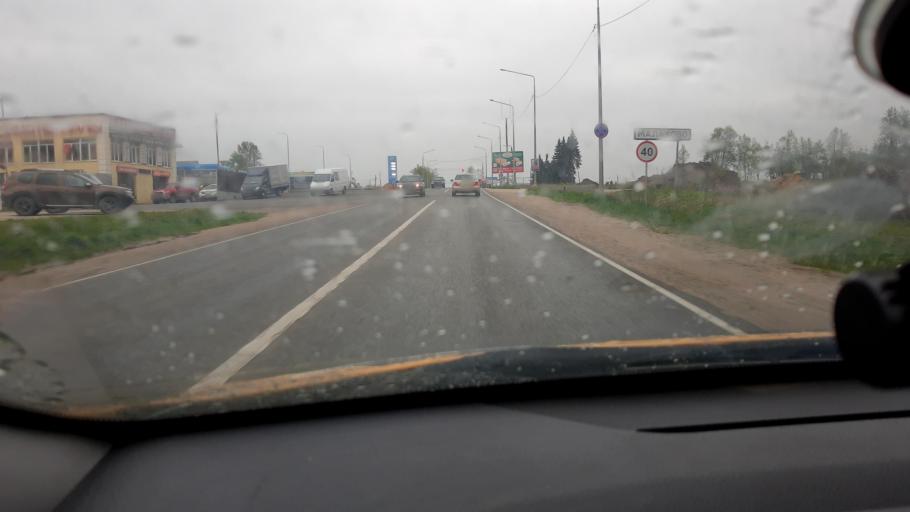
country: RU
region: Tula
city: Zaokskiy
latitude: 54.7498
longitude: 37.4387
